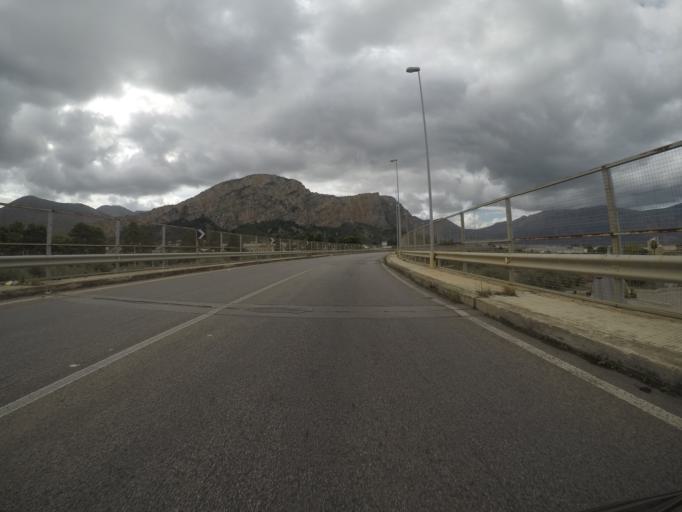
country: IT
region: Sicily
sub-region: Palermo
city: Capaci
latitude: 38.1670
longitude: 13.2218
